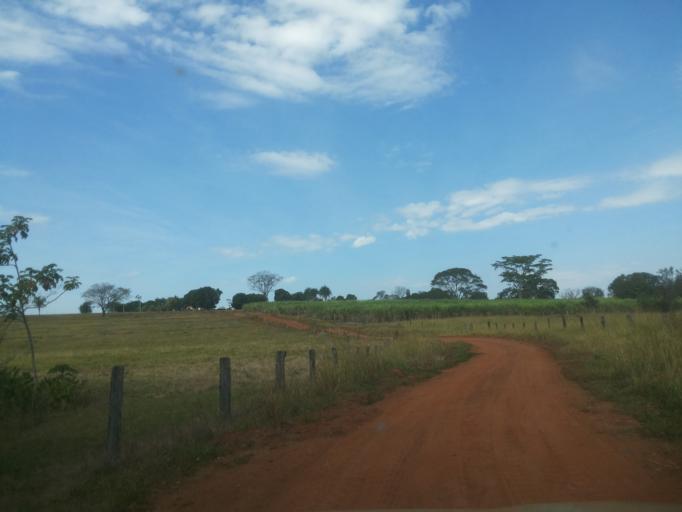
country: BR
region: Minas Gerais
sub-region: Ituiutaba
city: Ituiutaba
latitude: -19.0781
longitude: -49.3612
